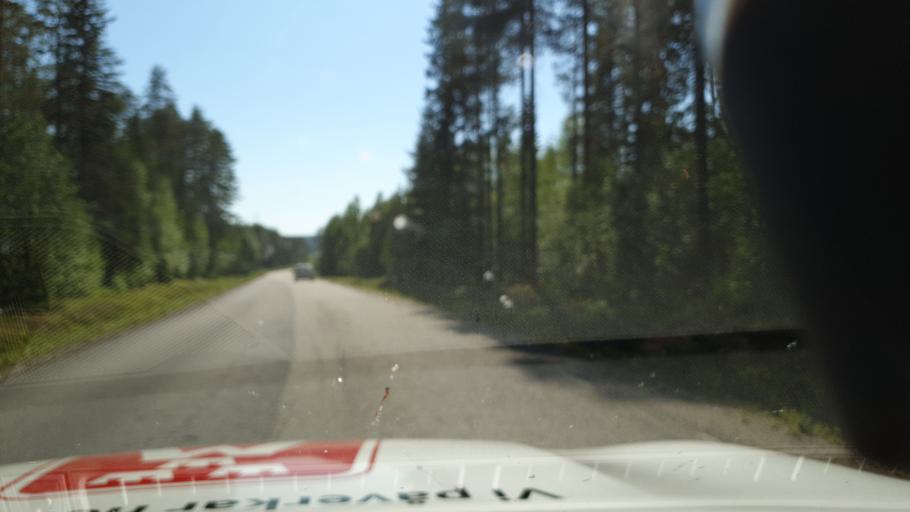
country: SE
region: Vaesterbotten
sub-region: Vindelns Kommun
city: Vindeln
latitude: 64.2363
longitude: 19.7962
